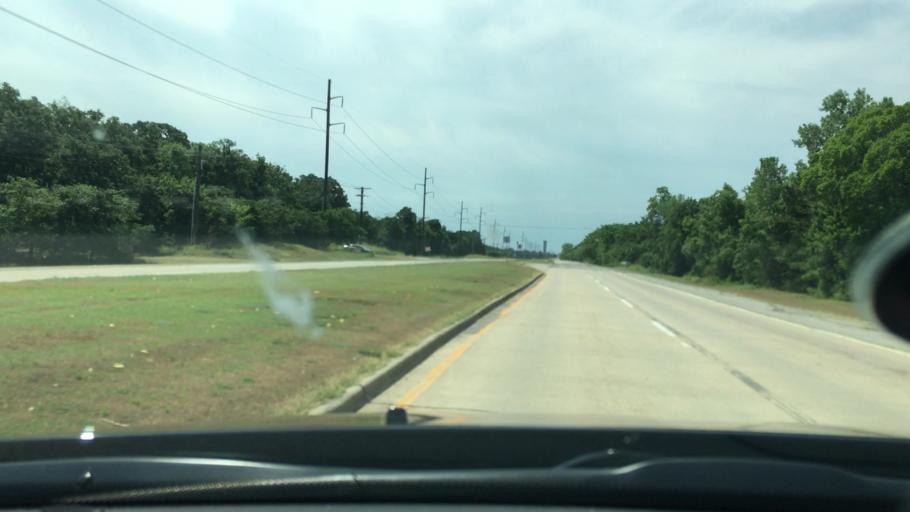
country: US
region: Oklahoma
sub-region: Carter County
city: Ardmore
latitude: 34.2179
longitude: -97.1432
